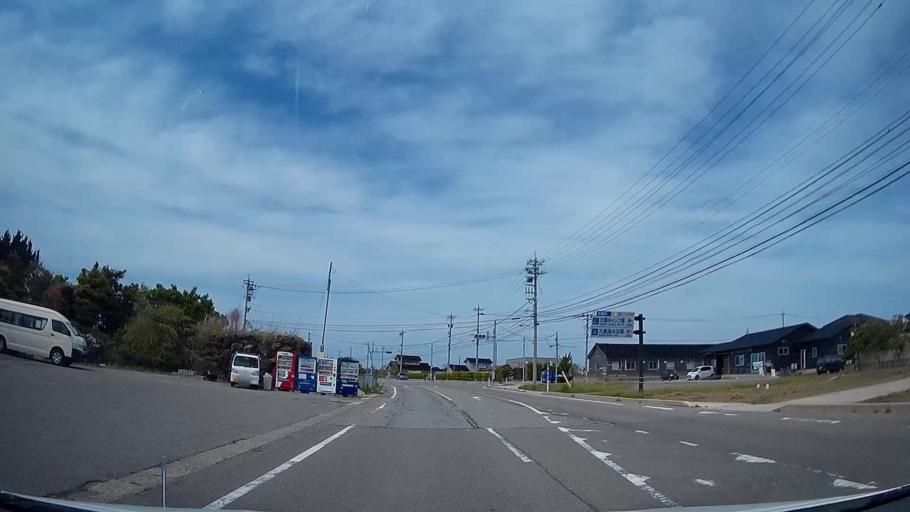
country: JP
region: Ishikawa
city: Hakui
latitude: 36.9781
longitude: 136.7765
